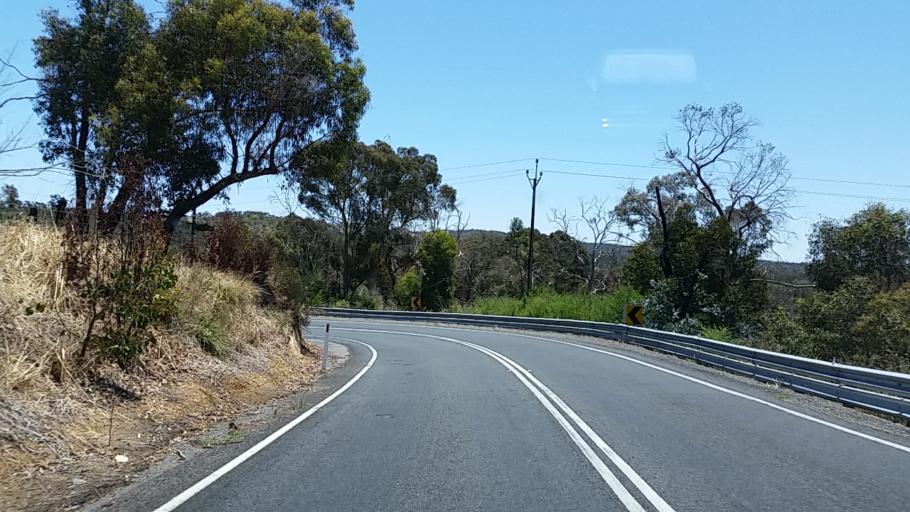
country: AU
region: South Australia
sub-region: Adelaide Hills
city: Gumeracha
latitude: -34.8220
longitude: 138.8346
